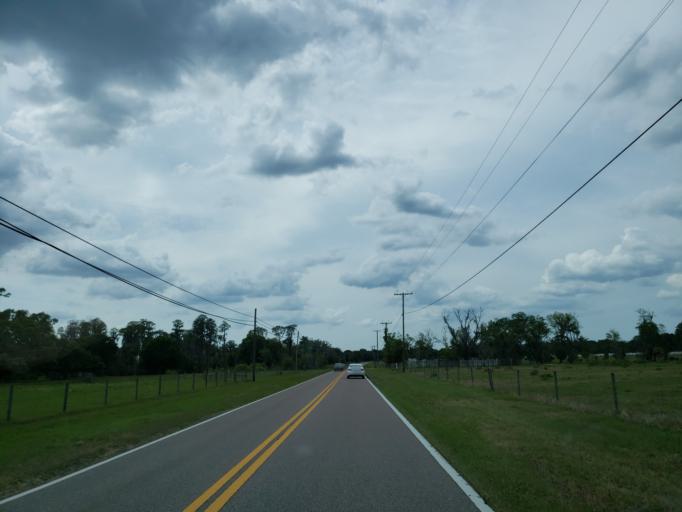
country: US
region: Florida
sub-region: Hillsborough County
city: Citrus Park
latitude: 28.1074
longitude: -82.5974
